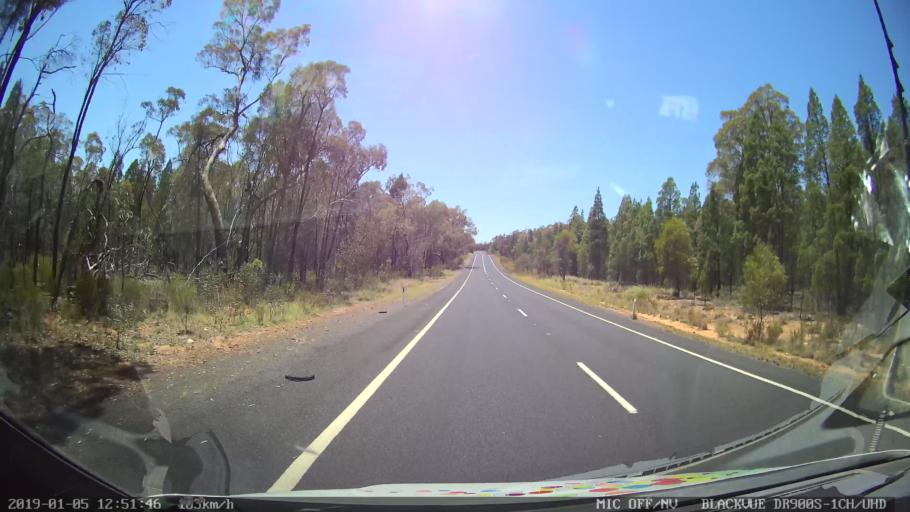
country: AU
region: New South Wales
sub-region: Warrumbungle Shire
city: Coonabarabran
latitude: -31.1214
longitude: 149.6450
